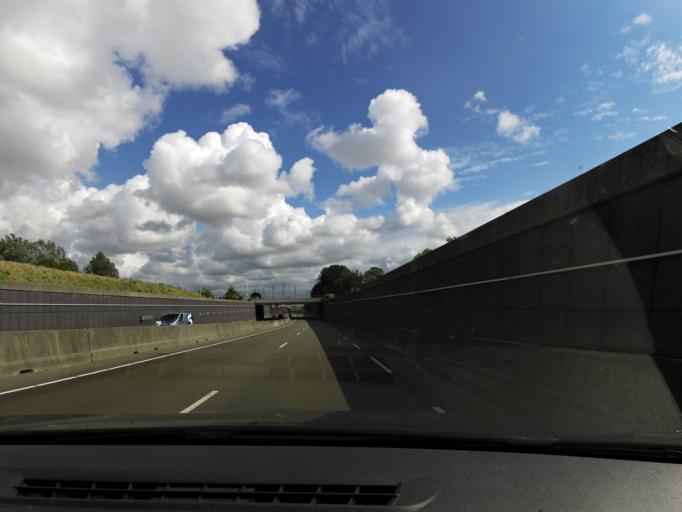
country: NL
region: South Holland
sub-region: Gemeente Westland
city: Kwintsheul
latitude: 52.0221
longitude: 4.2653
